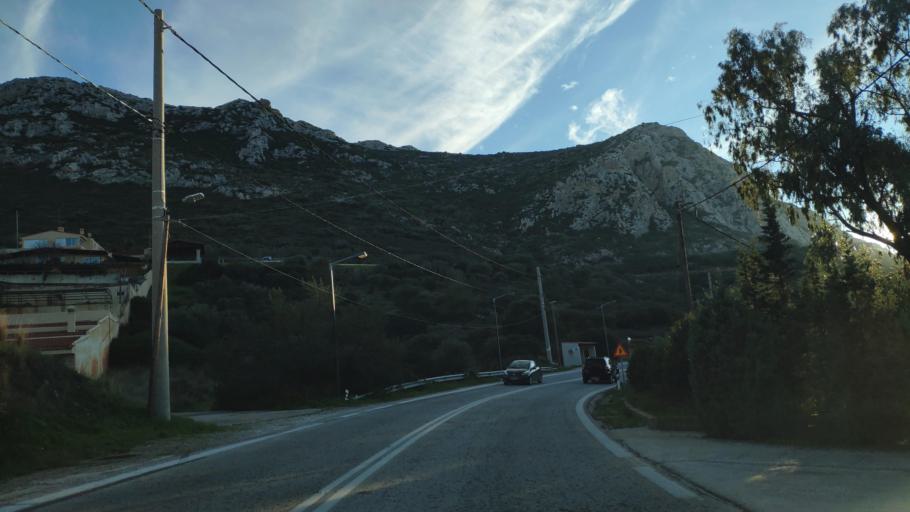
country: GR
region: Attica
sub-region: Nomarchia Anatolikis Attikis
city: Palaia Fokaia
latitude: 37.6785
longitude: 23.9461
